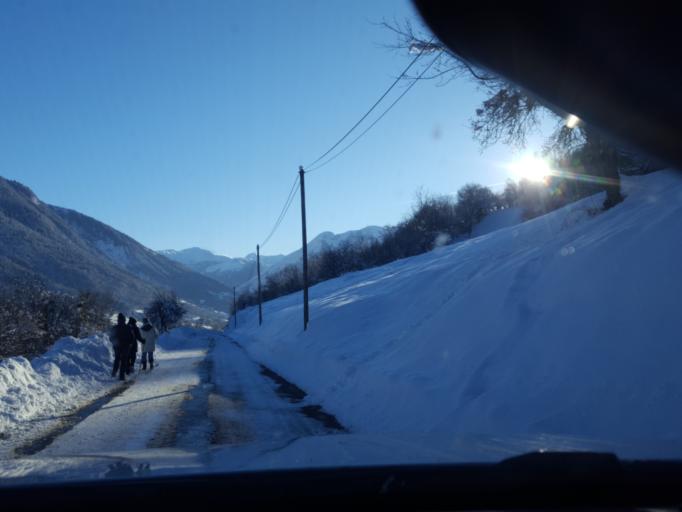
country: FR
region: Rhone-Alpes
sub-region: Departement de la Savoie
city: Salins-les-Thermes
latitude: 45.4635
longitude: 6.5107
